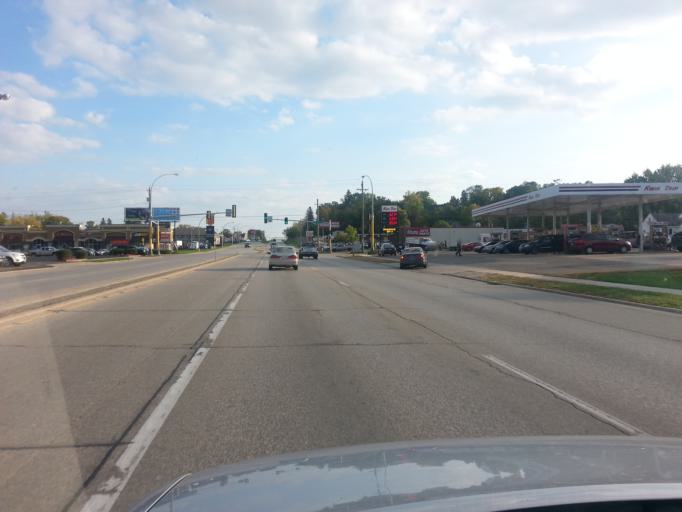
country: US
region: Minnesota
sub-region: Olmsted County
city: Rochester
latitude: 43.9936
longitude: -92.4629
